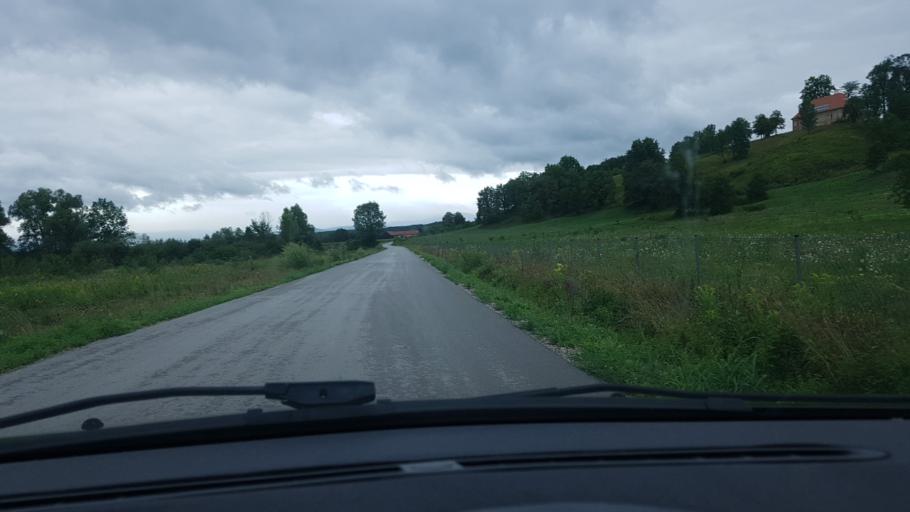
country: HR
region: Karlovacka
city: Ozalj
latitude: 45.5839
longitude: 15.5377
